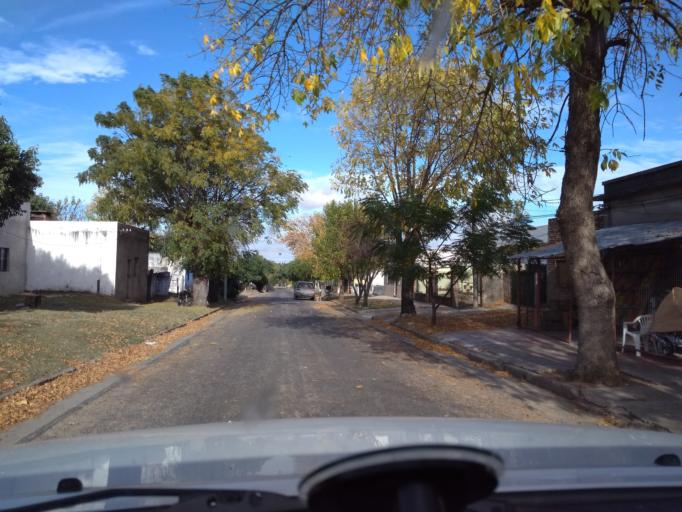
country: UY
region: Florida
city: Florida
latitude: -34.1054
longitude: -56.2133
